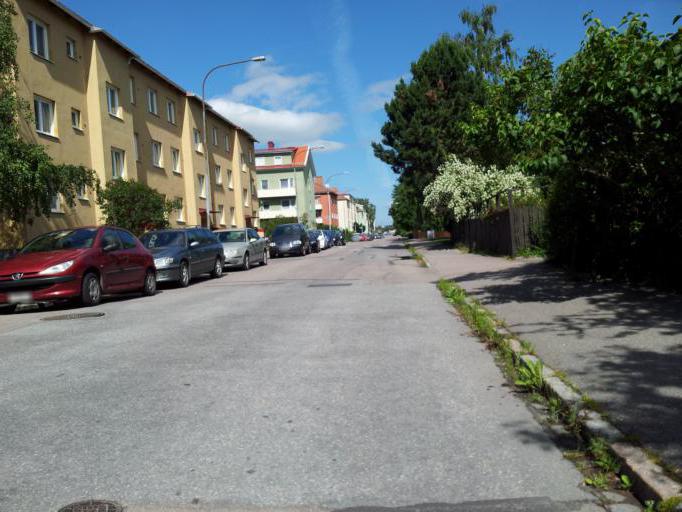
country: SE
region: Uppsala
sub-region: Uppsala Kommun
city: Uppsala
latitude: 59.8606
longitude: 17.6571
